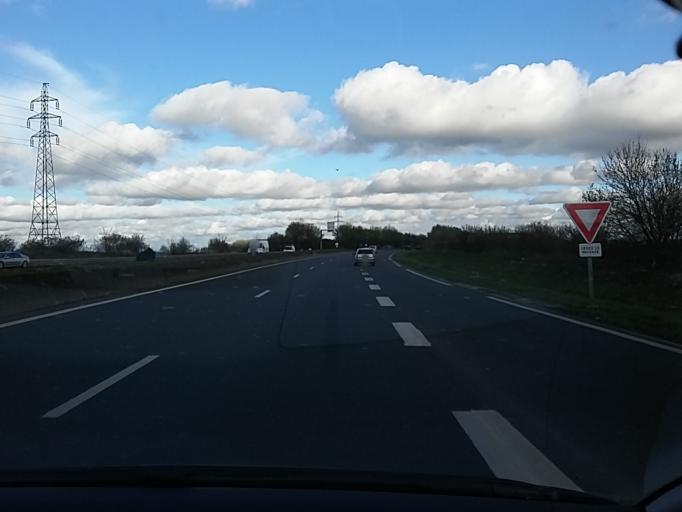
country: FR
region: Picardie
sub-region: Departement de la Somme
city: Camon
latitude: 49.9019
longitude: 2.3656
